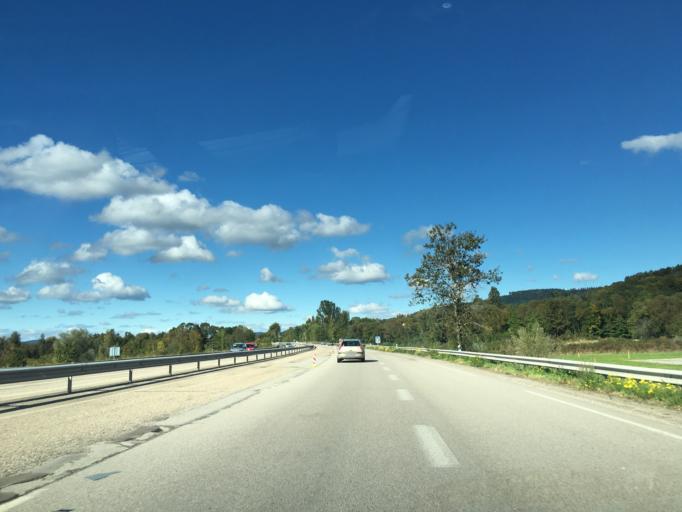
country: FR
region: Lorraine
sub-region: Departement des Vosges
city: Saint-Die-des-Vosges
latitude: 48.2948
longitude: 6.9308
